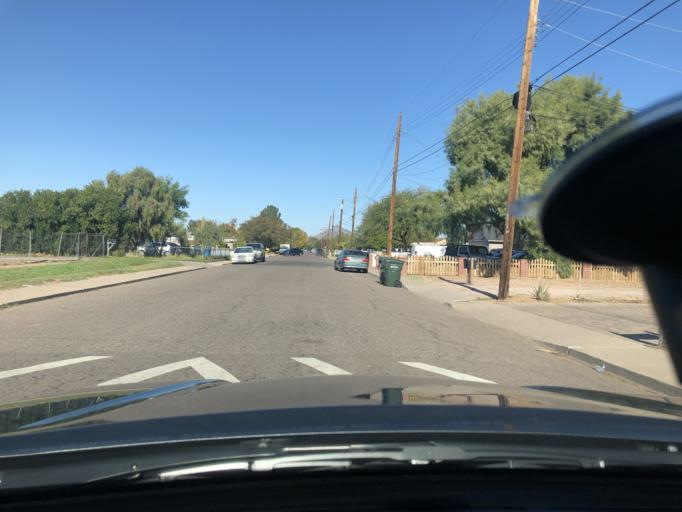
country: US
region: Arizona
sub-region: Maricopa County
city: Phoenix
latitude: 33.4679
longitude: -112.0266
